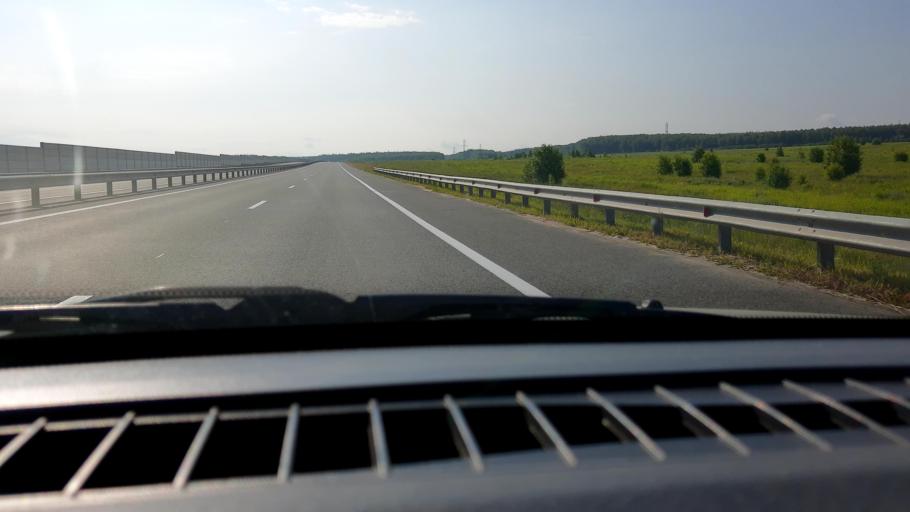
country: RU
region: Nizjnij Novgorod
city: Burevestnik
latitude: 56.1135
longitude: 43.9636
